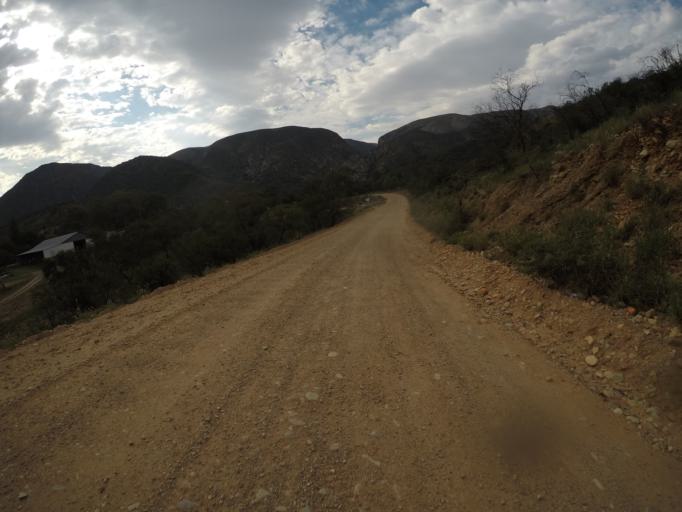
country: ZA
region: Eastern Cape
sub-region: Cacadu District Municipality
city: Kareedouw
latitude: -33.5852
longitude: 24.1653
